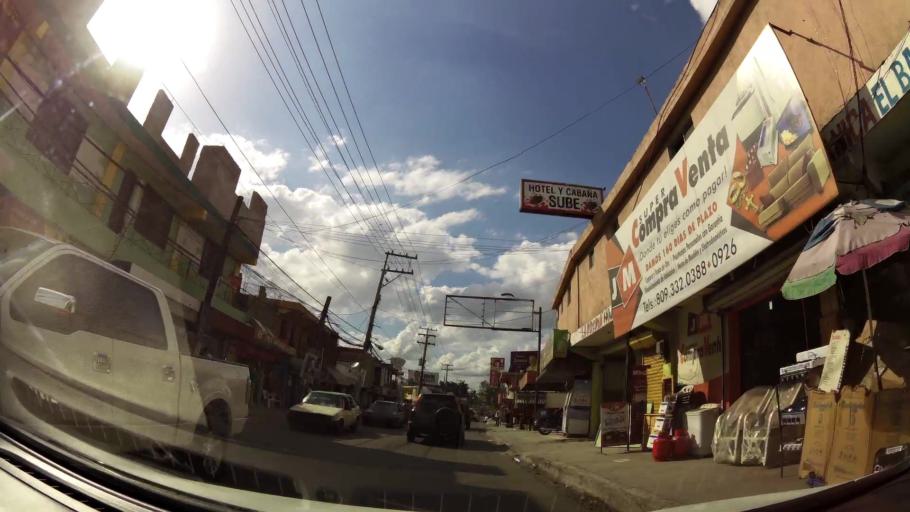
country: DO
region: Nacional
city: Ensanche Luperon
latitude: 18.5518
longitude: -69.9014
